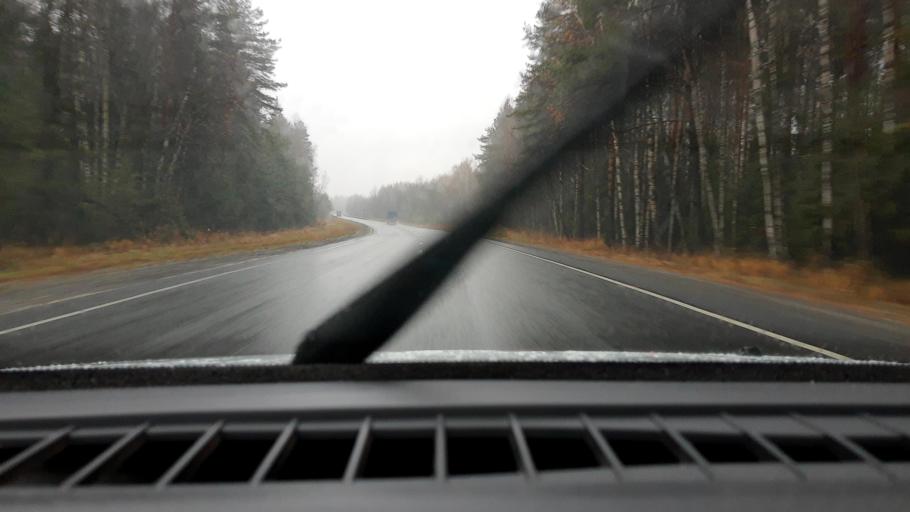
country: RU
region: Nizjnij Novgorod
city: Linda
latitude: 56.6657
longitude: 44.1336
